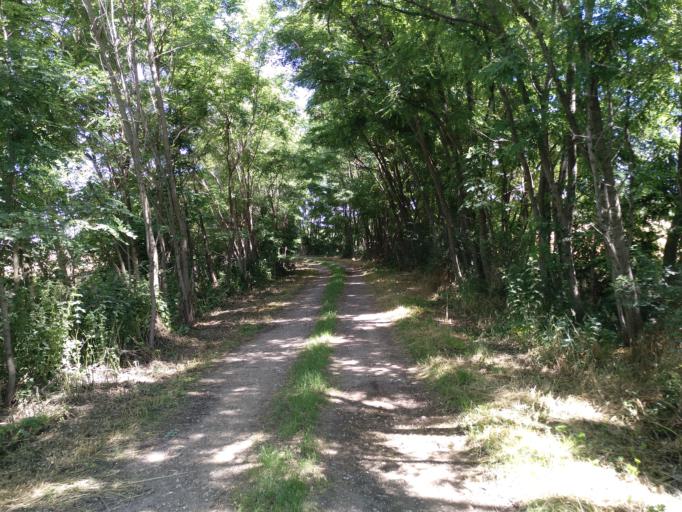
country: FR
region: Rhone-Alpes
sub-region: Departement du Rhone
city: Saint-Priest
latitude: 45.6893
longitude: 4.9629
